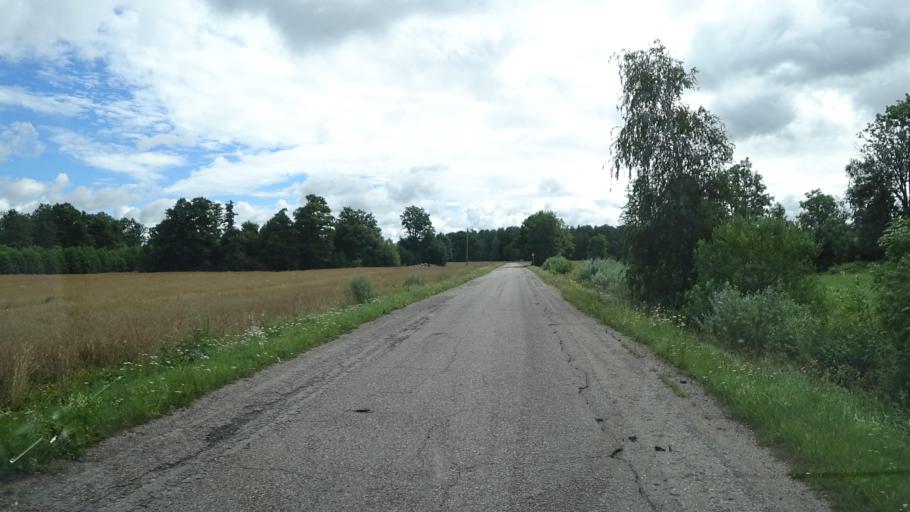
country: LV
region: Liepaja
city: Vec-Liepaja
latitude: 56.6582
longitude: 21.0869
